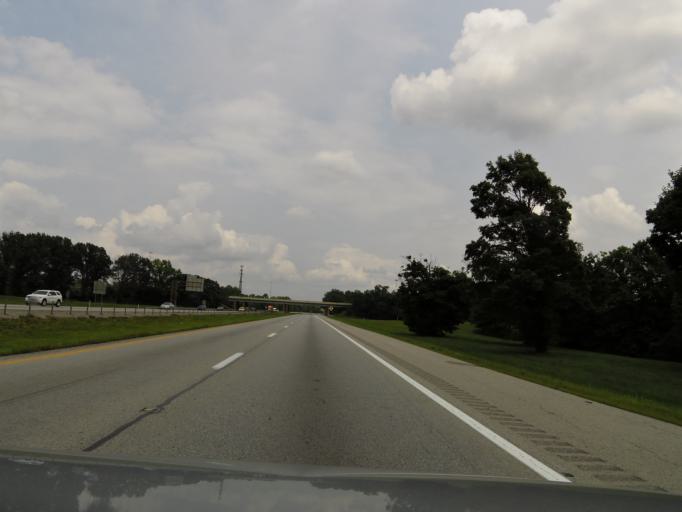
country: US
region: Kentucky
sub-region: Jefferson County
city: Worthington
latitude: 38.3133
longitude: -85.5846
